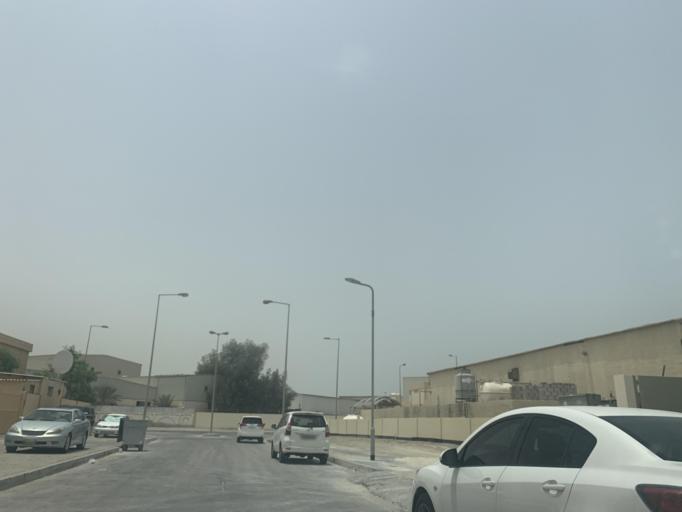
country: BH
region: Northern
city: Sitrah
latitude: 26.1821
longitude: 50.6105
